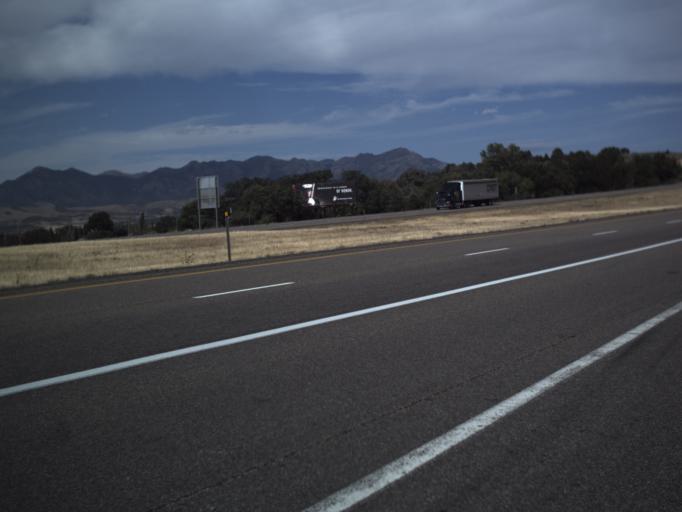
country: US
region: Utah
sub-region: Millard County
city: Fillmore
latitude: 39.0866
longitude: -112.2728
